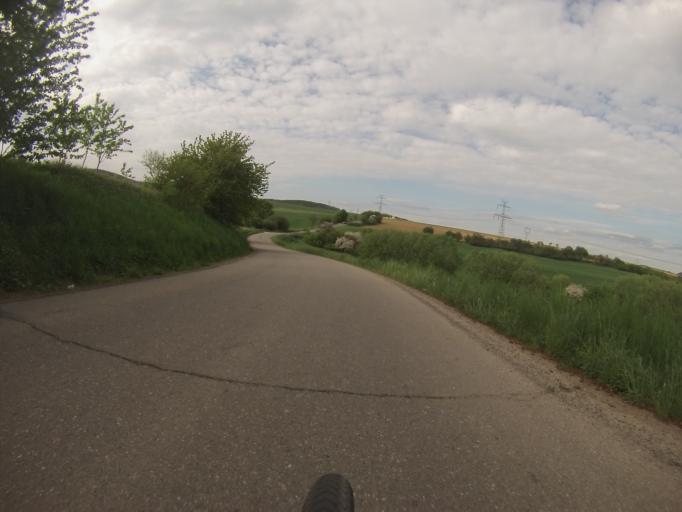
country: CZ
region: South Moravian
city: Veverska Bityska
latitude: 49.2835
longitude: 16.4439
